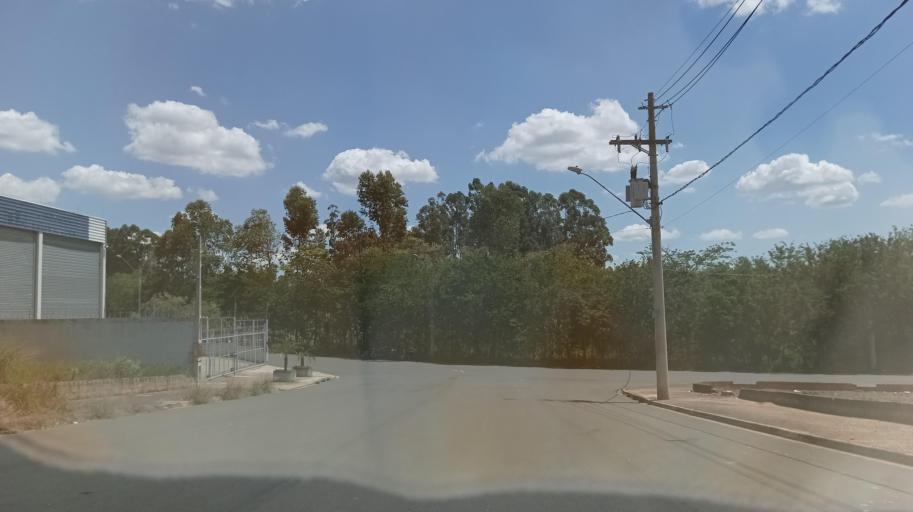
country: BR
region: Sao Paulo
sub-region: Sorocaba
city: Sorocaba
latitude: -23.4657
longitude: -47.4569
